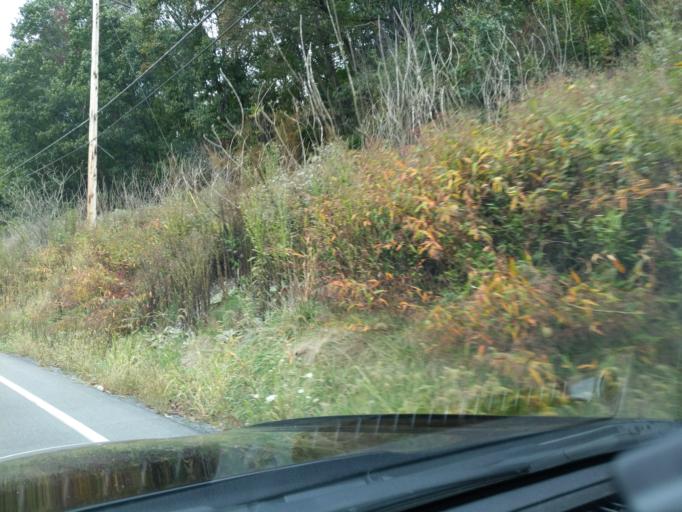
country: US
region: Pennsylvania
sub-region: Blair County
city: Altoona
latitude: 40.4899
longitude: -78.4379
